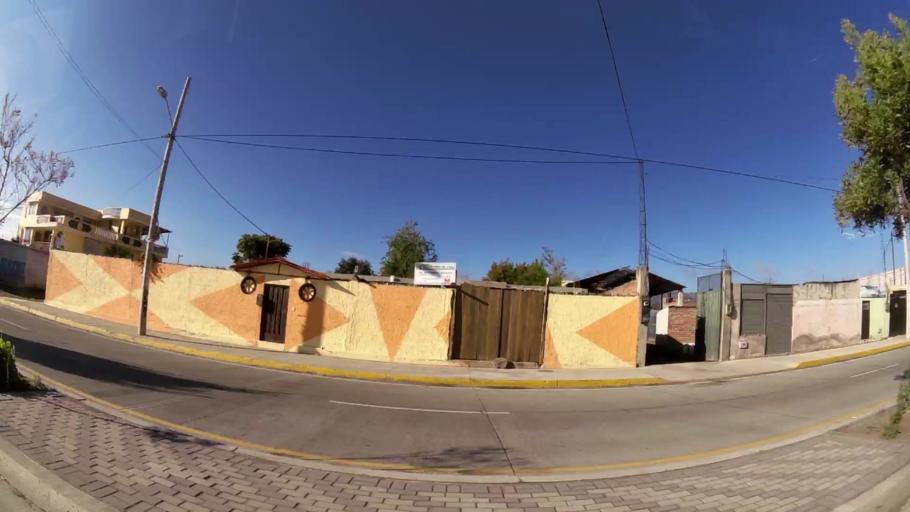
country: EC
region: Chimborazo
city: Riobamba
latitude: -1.6884
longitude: -78.6390
